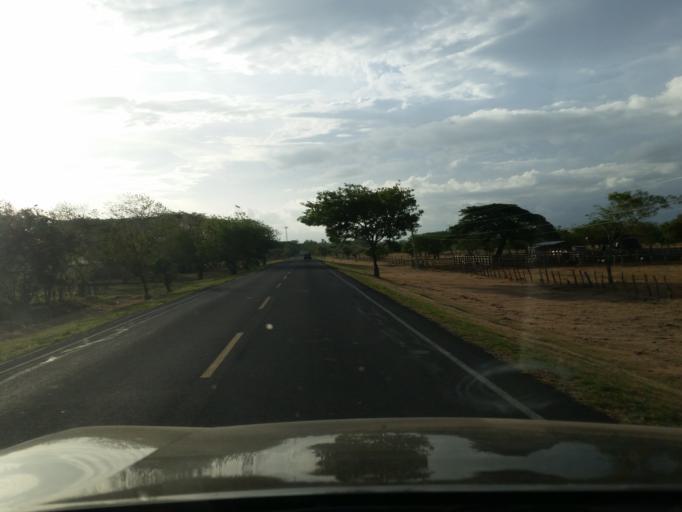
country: NI
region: Rivas
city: Belen
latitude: 11.6100
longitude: -85.9402
